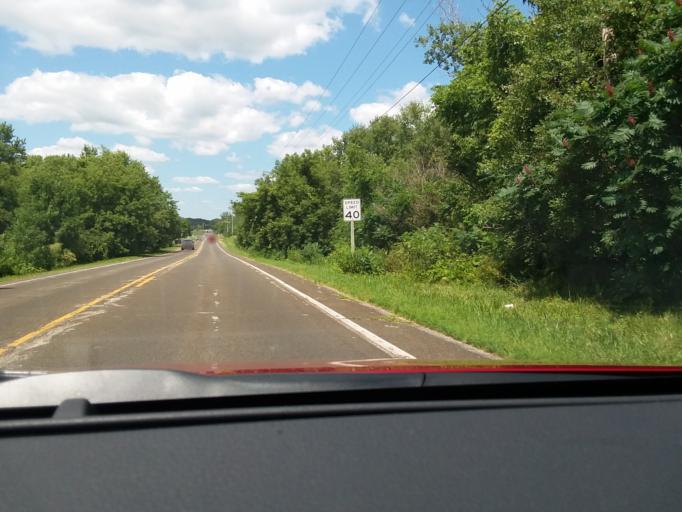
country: US
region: Wisconsin
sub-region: Dane County
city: Windsor
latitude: 43.2207
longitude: -89.3434
